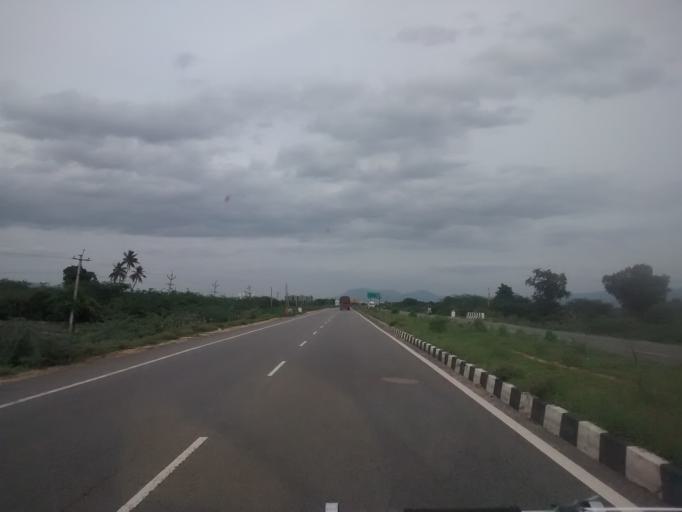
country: IN
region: Andhra Pradesh
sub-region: Chittoor
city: Tirupati
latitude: 13.6040
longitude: 79.3803
